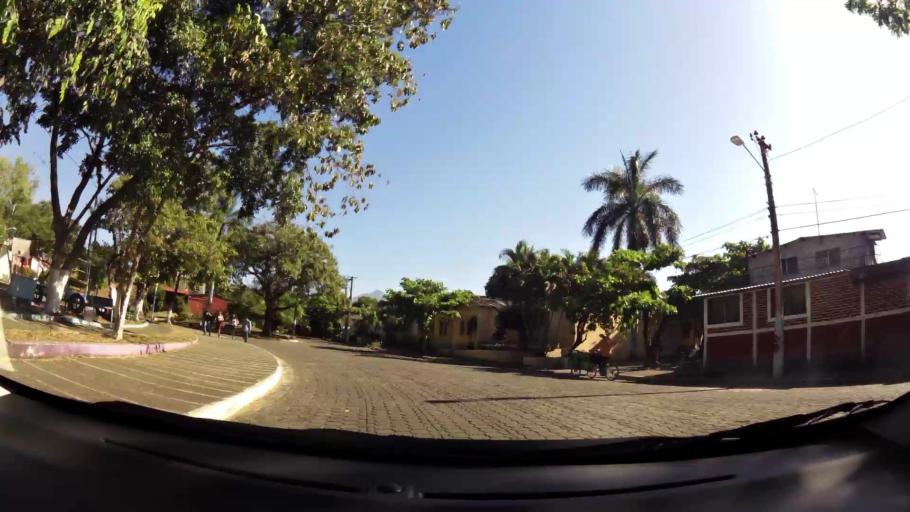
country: SV
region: Sonsonate
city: Sonzacate
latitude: 13.7285
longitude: -89.7202
